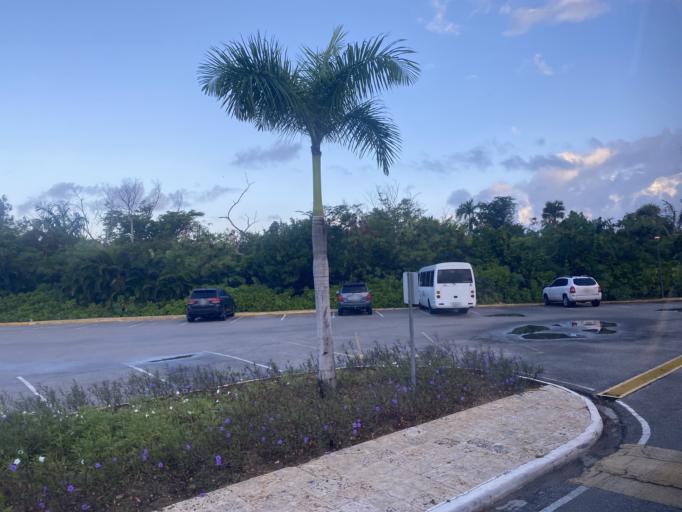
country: DO
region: San Juan
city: Punta Cana
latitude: 18.7300
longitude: -68.4693
